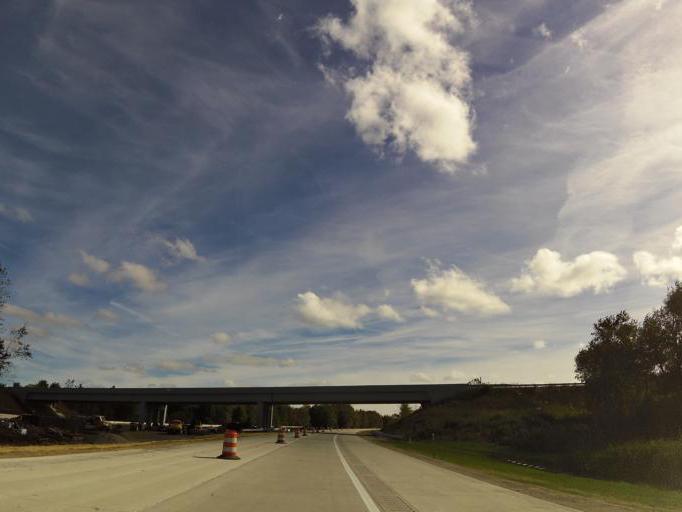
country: US
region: Michigan
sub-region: Saint Clair County
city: Marysville
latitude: 42.9879
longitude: -82.5860
